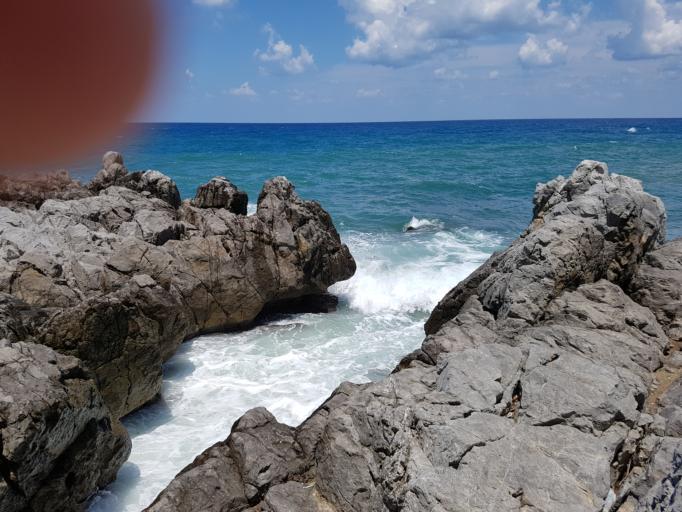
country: IT
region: Sicily
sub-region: Palermo
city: Cefalu
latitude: 38.0411
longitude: 14.0233
